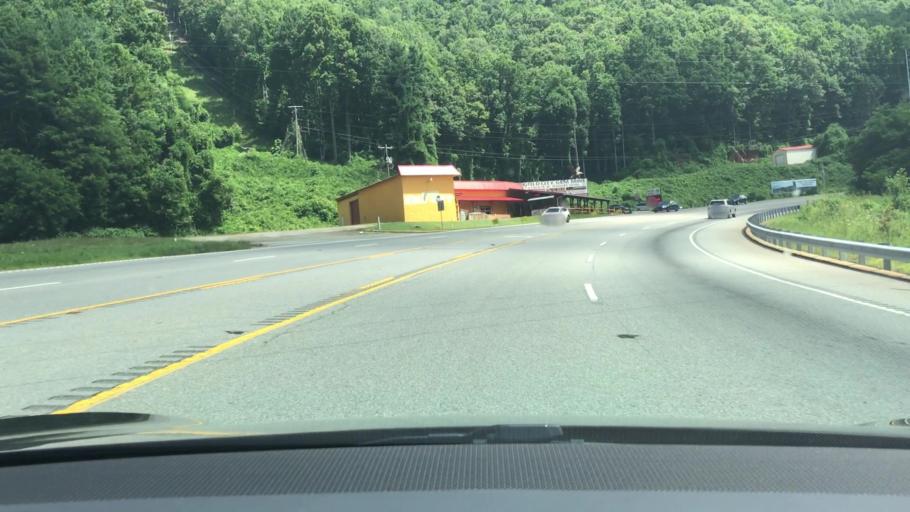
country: US
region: North Carolina
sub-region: Macon County
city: Franklin
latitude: 35.2588
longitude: -83.3163
